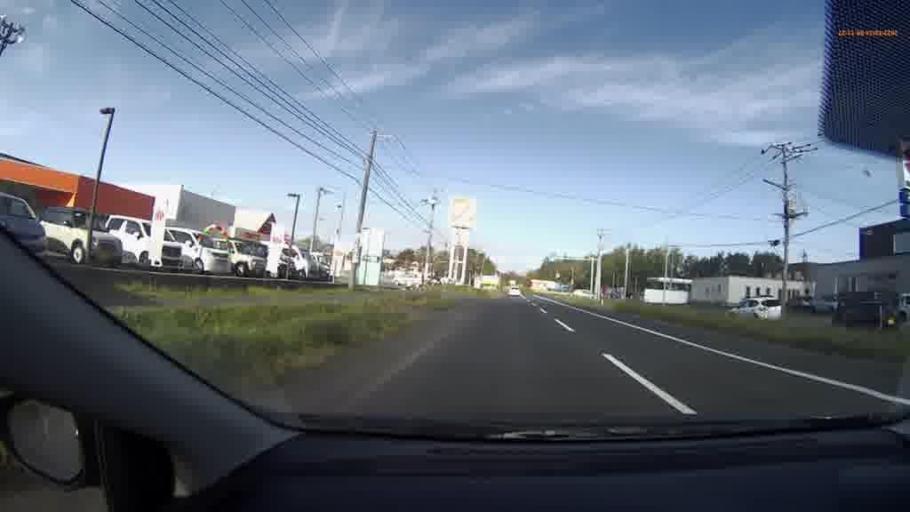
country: JP
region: Hokkaido
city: Kushiro
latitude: 43.0134
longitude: 144.4068
